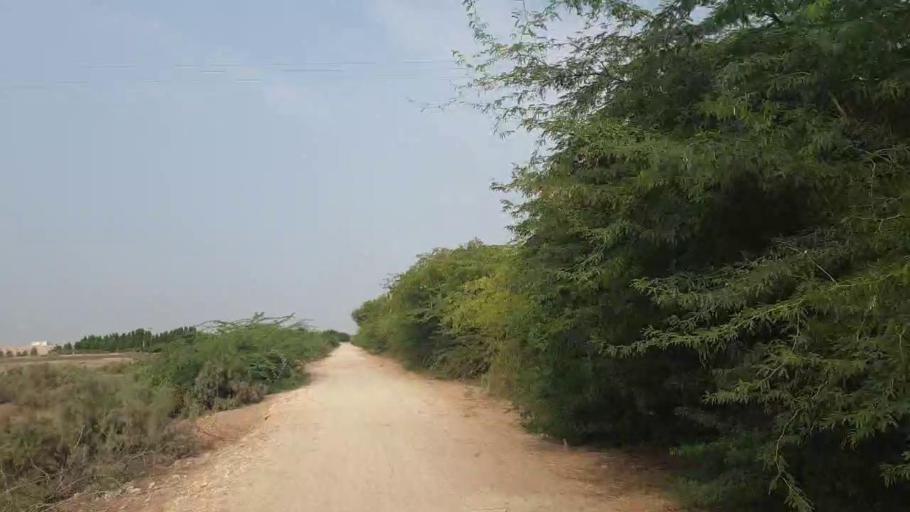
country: PK
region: Sindh
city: Badin
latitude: 24.6005
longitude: 68.7413
